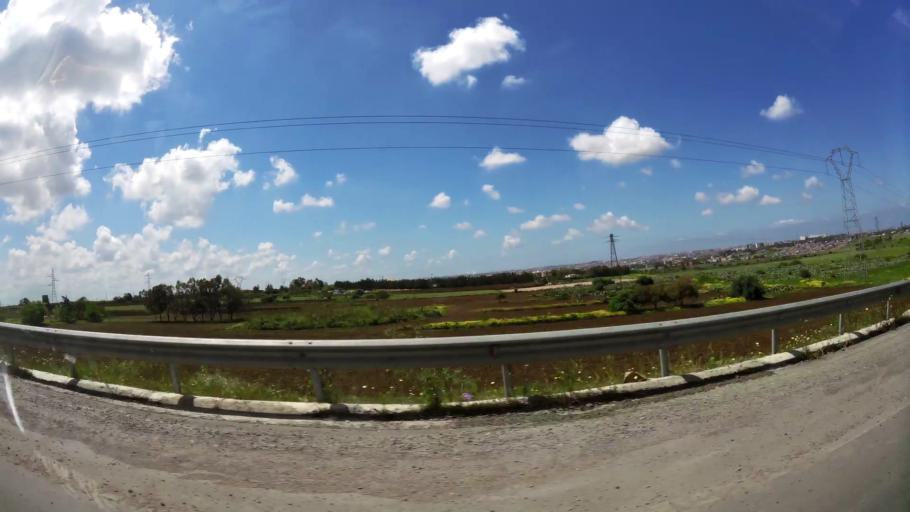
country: MA
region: Grand Casablanca
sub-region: Nouaceur
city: Bouskoura
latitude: 33.5112
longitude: -7.6130
